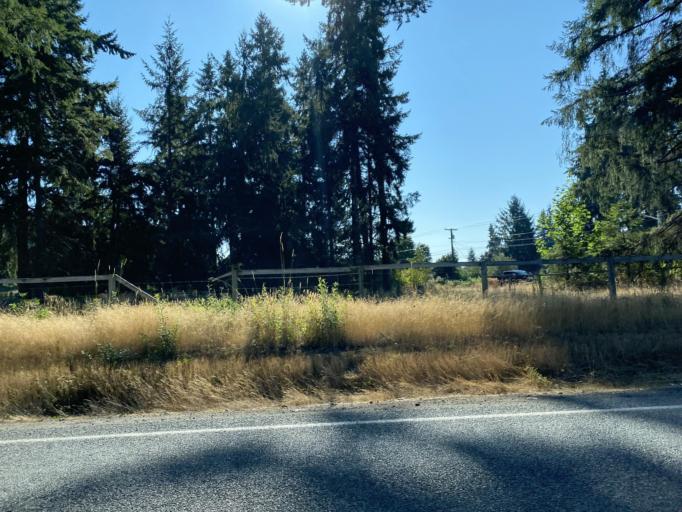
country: US
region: Washington
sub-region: Thurston County
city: Tanglewilde-Thompson Place
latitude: 46.9860
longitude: -122.7406
